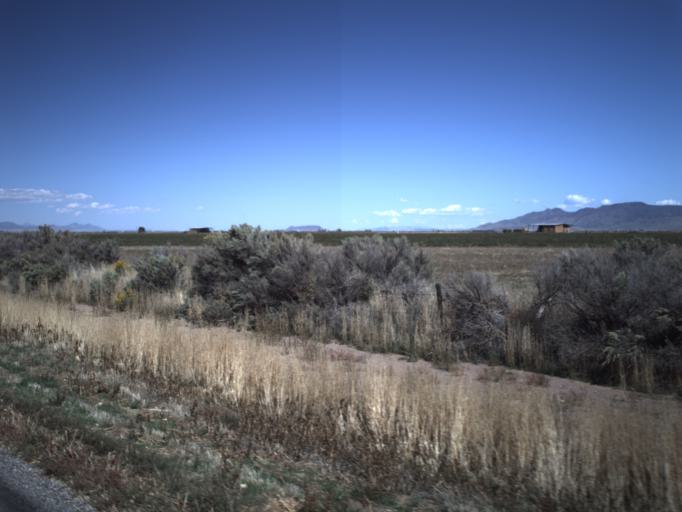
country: US
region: Utah
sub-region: Washington County
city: Enterprise
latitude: 37.6200
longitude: -113.6612
